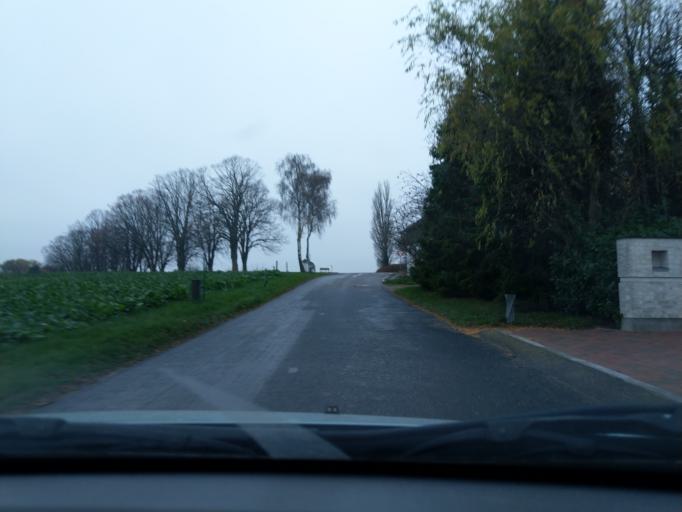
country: DK
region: Zealand
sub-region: Vordingborg Kommune
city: Praesto
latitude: 55.1073
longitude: 12.0786
